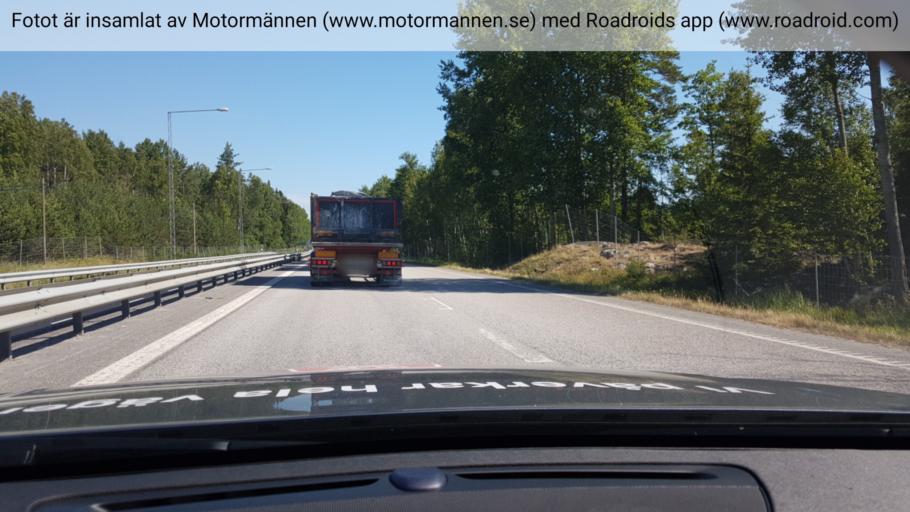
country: SE
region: Stockholm
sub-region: Vallentuna Kommun
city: Vallentuna
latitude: 59.5007
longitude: 18.1672
